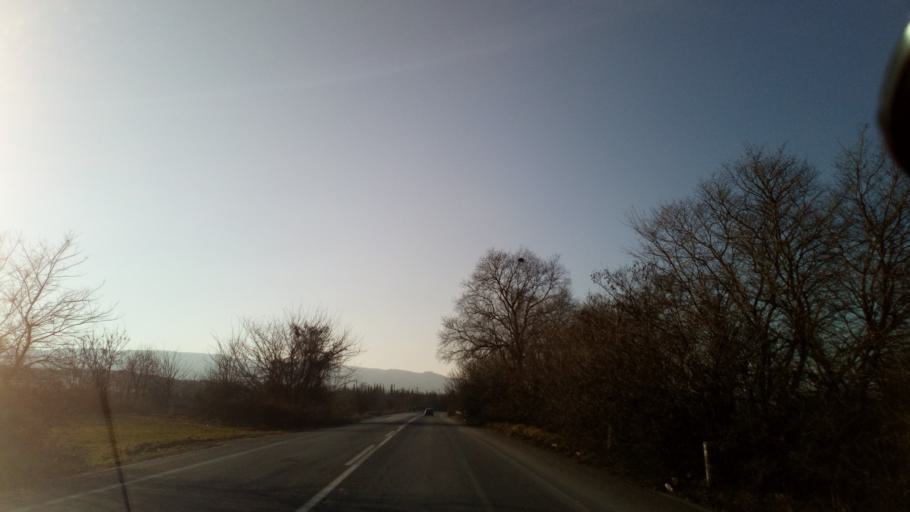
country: GR
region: Central Macedonia
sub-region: Nomos Thessalonikis
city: Agios Vasileios
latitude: 40.6566
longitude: 23.1372
